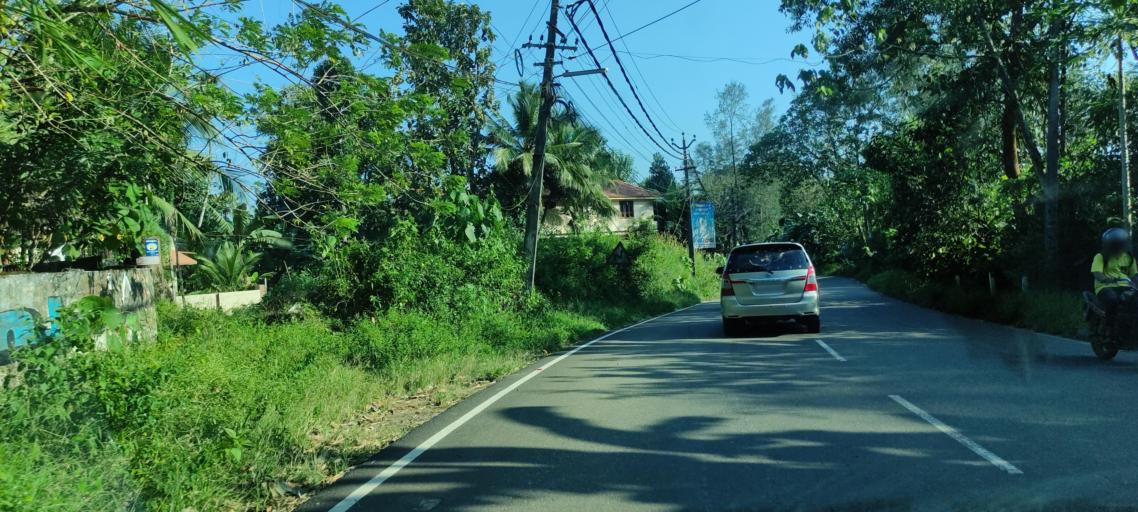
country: IN
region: Kerala
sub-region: Pattanamtitta
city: Adur
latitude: 9.1644
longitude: 76.7430
